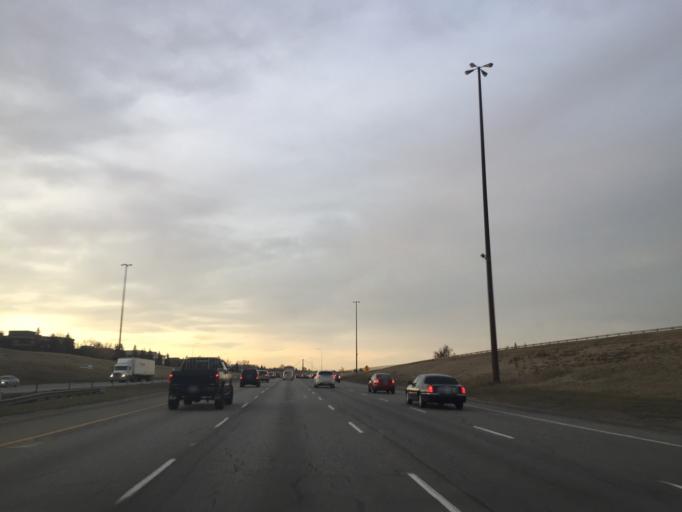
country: CA
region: Alberta
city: Calgary
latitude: 51.0812
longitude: -114.0340
